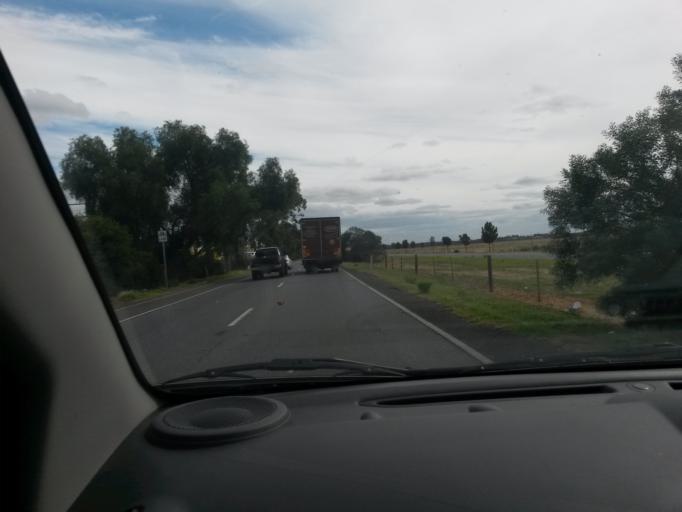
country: AU
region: South Australia
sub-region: Salisbury
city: Salisbury
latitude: -34.7972
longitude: 138.6422
